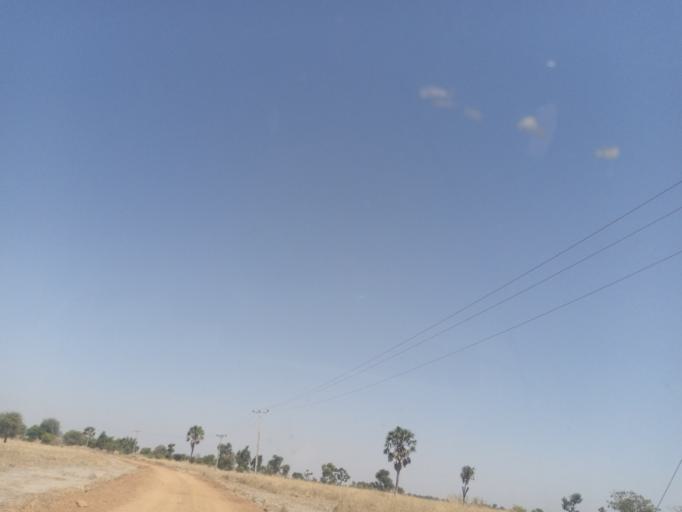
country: NG
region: Adamawa
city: Yola
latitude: 9.3026
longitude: 12.8893
